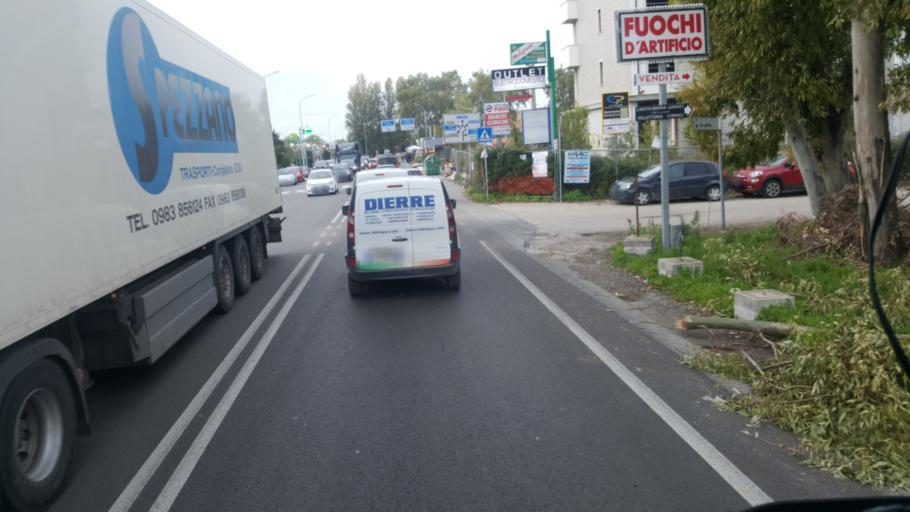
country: IT
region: Latium
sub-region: Provincia di Latina
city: Borgo Podgora
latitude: 41.4810
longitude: 12.8663
